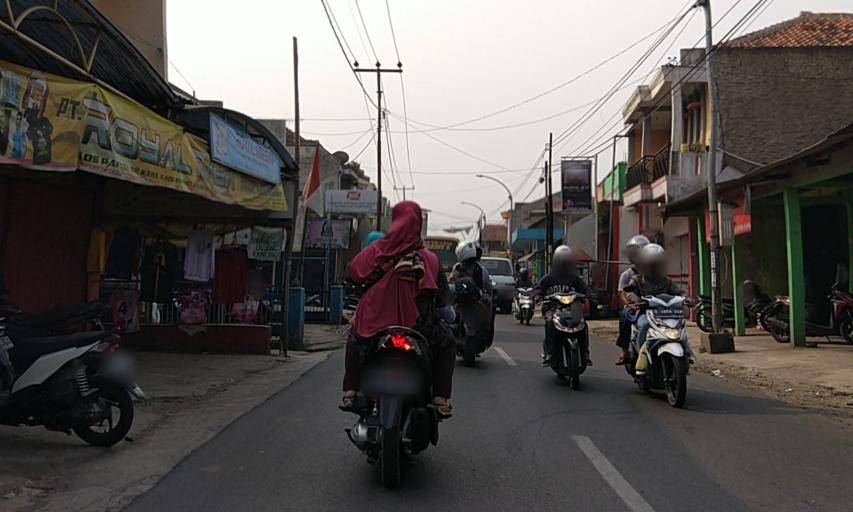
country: ID
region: West Java
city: Margahayukencana
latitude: -6.9467
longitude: 107.5645
